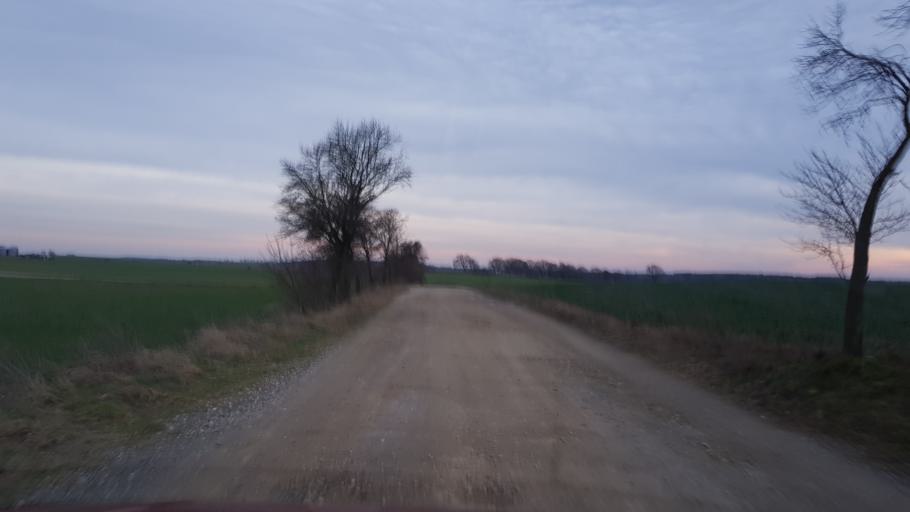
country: PL
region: West Pomeranian Voivodeship
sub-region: Powiat choszczenski
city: Pelczyce
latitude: 53.0345
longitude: 15.2607
